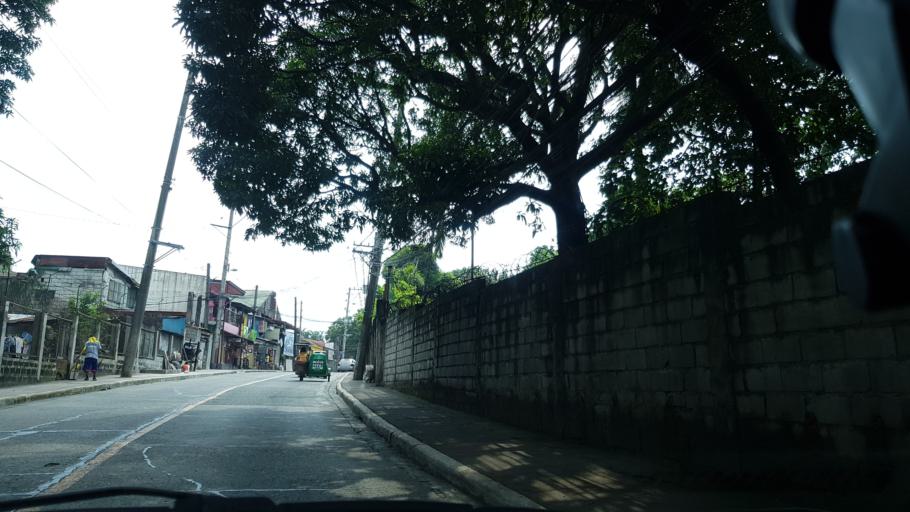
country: PH
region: Calabarzon
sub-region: Province of Rizal
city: Antipolo
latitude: 14.6567
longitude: 121.1249
